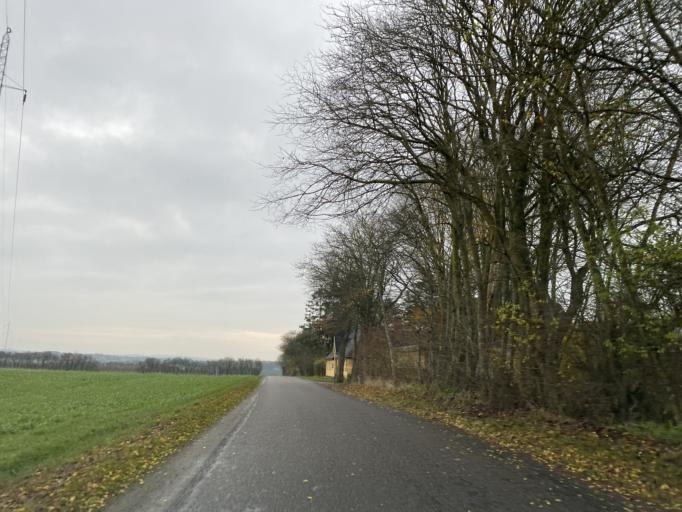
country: DK
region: Central Jutland
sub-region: Silkeborg Kommune
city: Svejbaek
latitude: 56.1669
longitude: 9.6620
